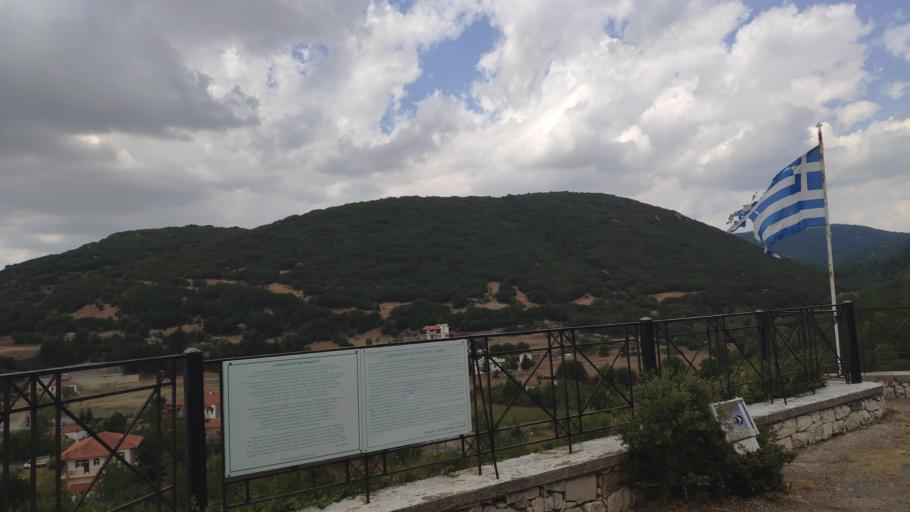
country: GR
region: Peloponnese
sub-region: Nomos Lakonias
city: Kariai
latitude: 37.2914
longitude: 22.4978
